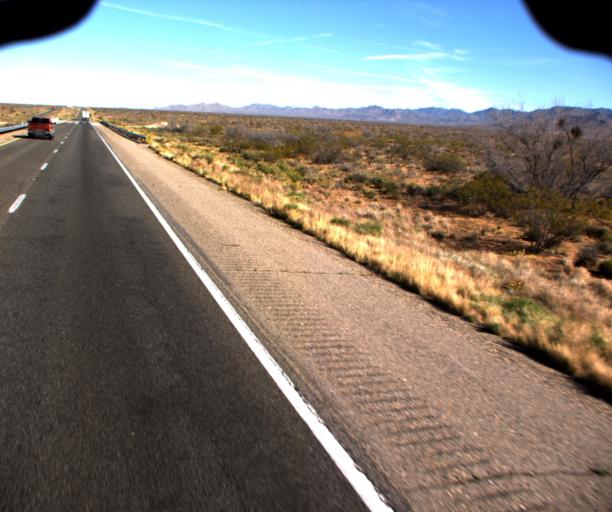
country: US
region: Arizona
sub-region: Mohave County
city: Golden Valley
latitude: 35.3019
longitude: -114.1904
